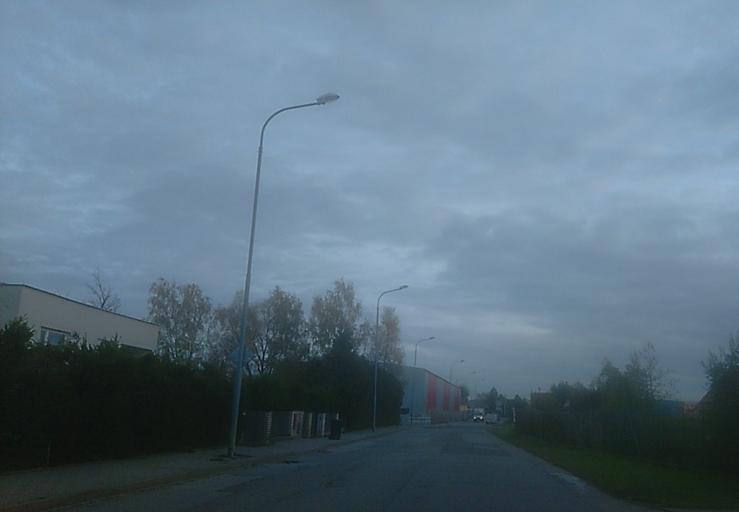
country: CZ
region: Jihocesky
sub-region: Okres Ceske Budejovice
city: Ceske Budejovice
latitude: 48.9733
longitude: 14.5086
